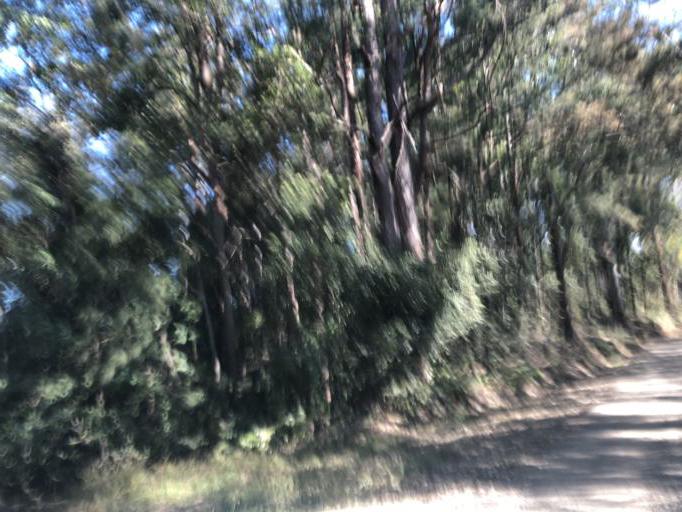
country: AU
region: New South Wales
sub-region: Bellingen
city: Bellingen
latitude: -30.4343
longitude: 152.8353
